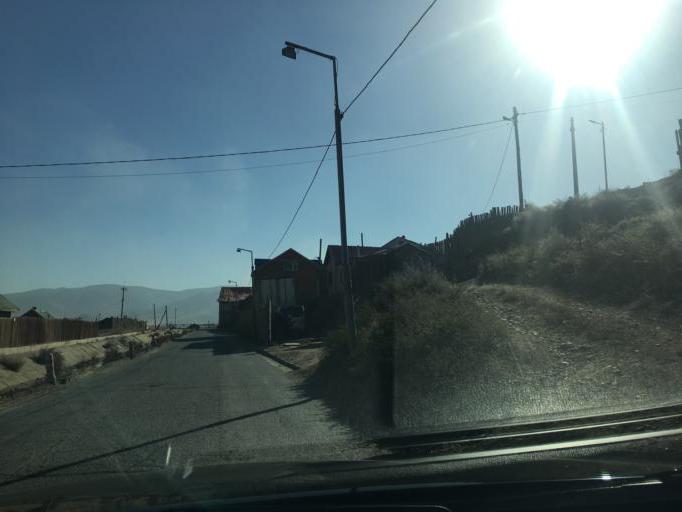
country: MN
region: Ulaanbaatar
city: Ulaanbaatar
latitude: 47.9357
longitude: 106.8822
